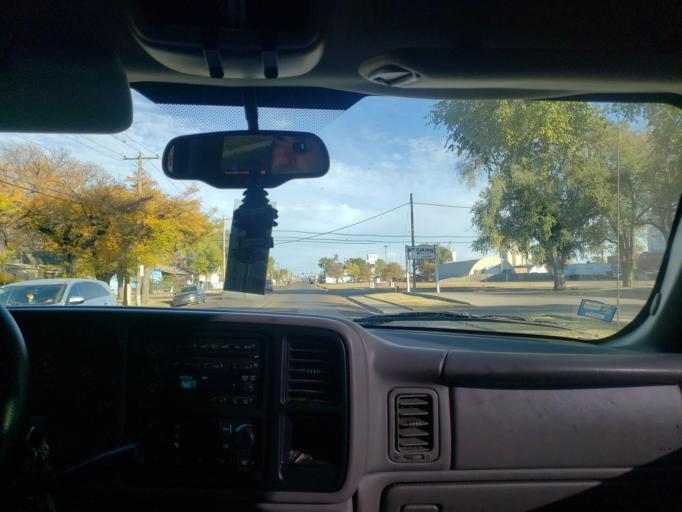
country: US
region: Kansas
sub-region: Finney County
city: Garden City
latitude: 37.9667
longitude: -100.8802
